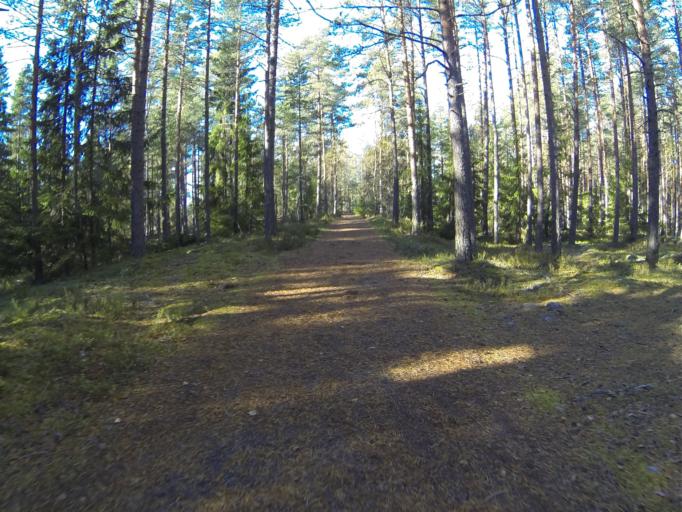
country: FI
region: Varsinais-Suomi
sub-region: Salo
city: Saerkisalo
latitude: 60.1978
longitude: 22.9298
